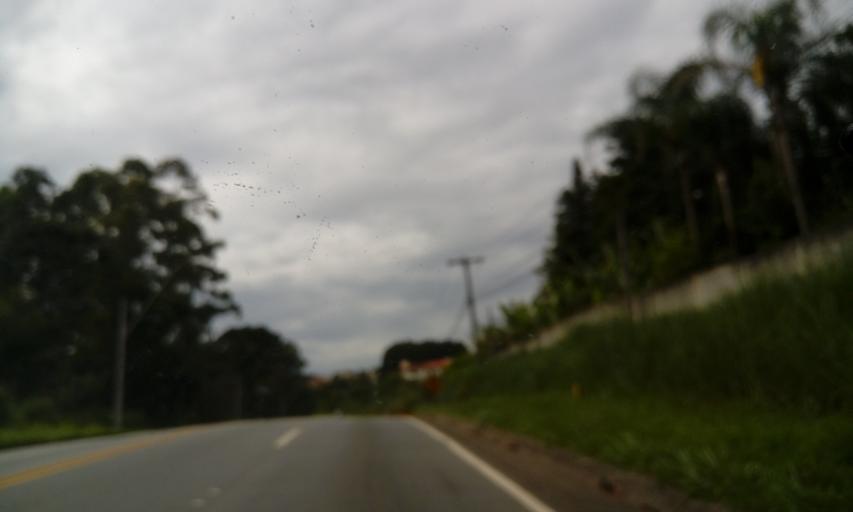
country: BR
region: Sao Paulo
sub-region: Caieiras
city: Caieiras
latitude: -23.3728
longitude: -46.7497
